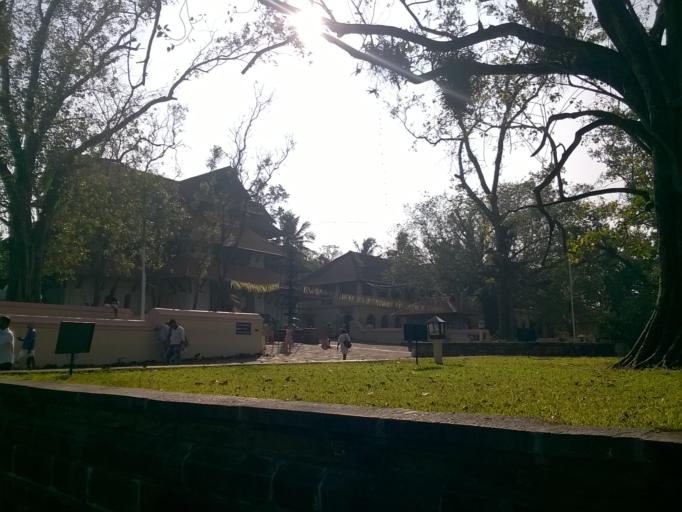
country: IN
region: Kerala
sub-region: Thrissur District
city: Trichur
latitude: 10.5247
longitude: 76.2131
